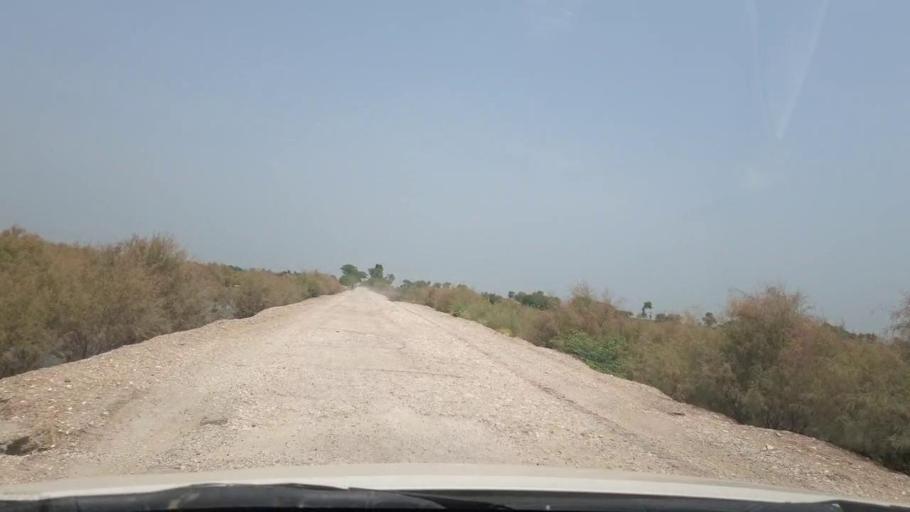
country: PK
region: Sindh
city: Rustam jo Goth
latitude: 28.0407
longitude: 68.8146
